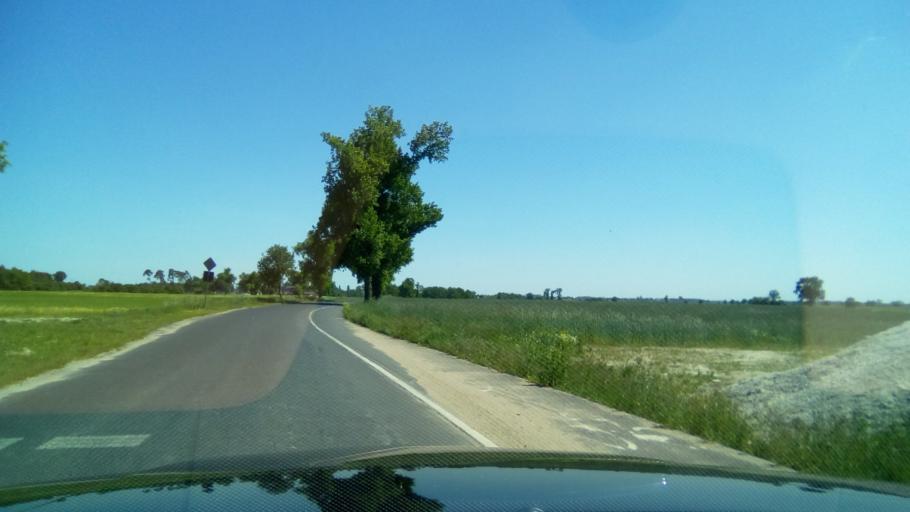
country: PL
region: Greater Poland Voivodeship
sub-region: Powiat gnieznienski
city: Gniezno
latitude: 52.4659
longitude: 17.5591
